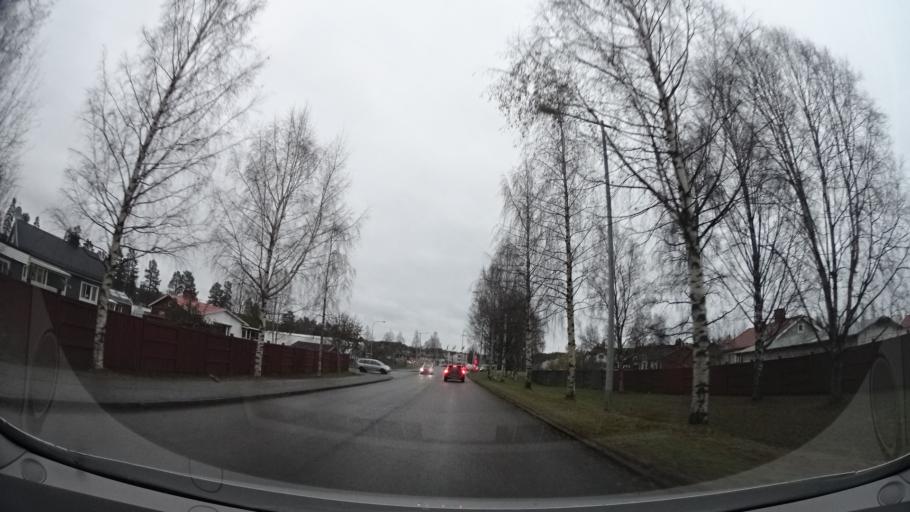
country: SE
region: Vaesterbotten
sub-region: Skelleftea Kommun
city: Skelleftea
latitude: 64.7582
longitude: 20.9611
